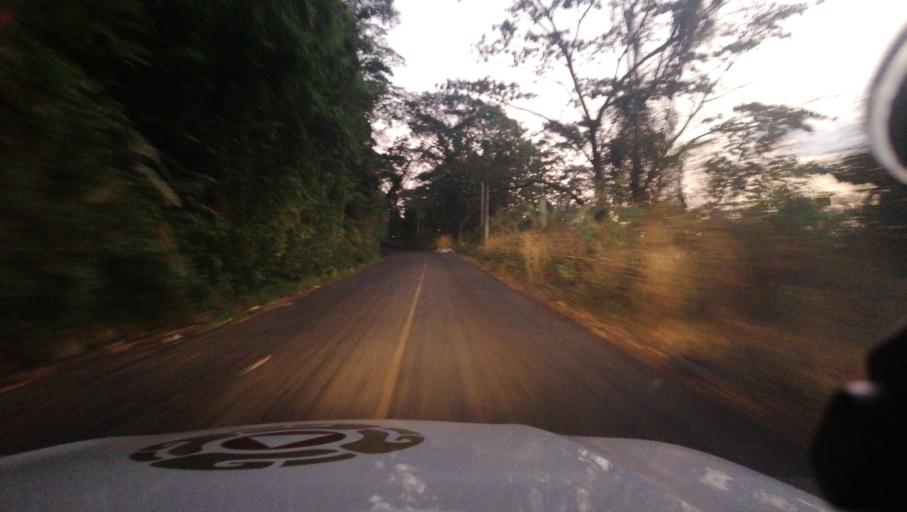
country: MX
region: Chiapas
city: Veinte de Noviembre
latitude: 14.9686
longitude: -92.2522
